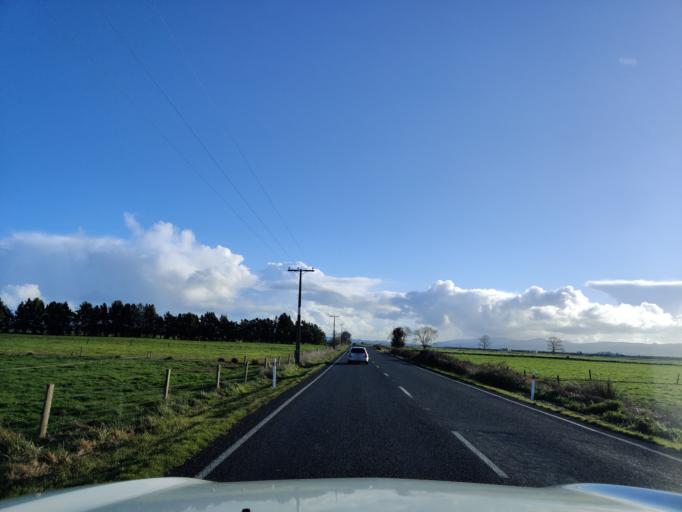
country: NZ
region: Waikato
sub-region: Hauraki District
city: Paeroa
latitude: -37.4909
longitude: 175.6004
